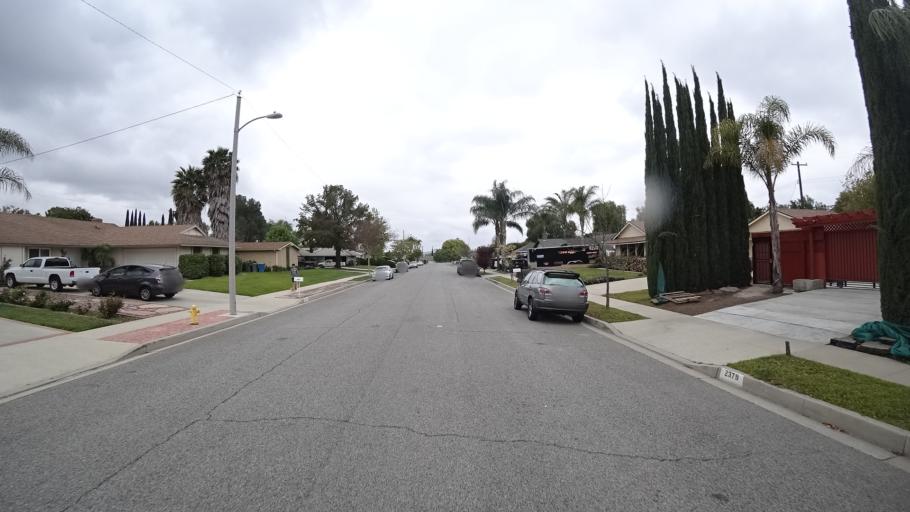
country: US
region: California
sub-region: Ventura County
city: Thousand Oaks
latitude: 34.2156
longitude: -118.8809
